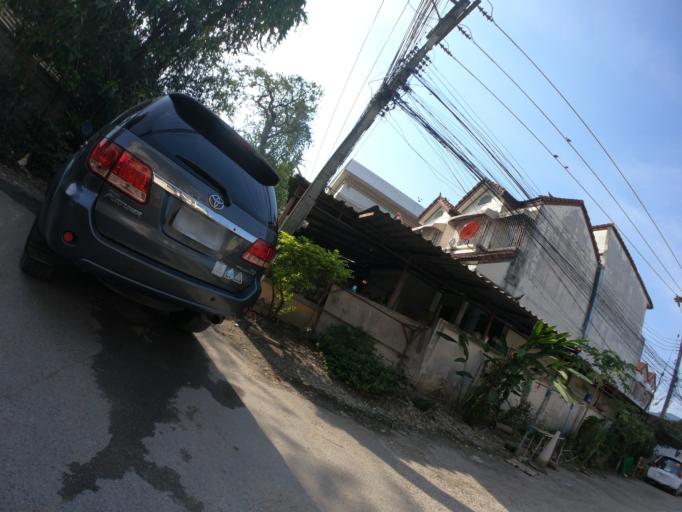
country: TH
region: Chiang Mai
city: Chiang Mai
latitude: 18.8190
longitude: 98.9839
